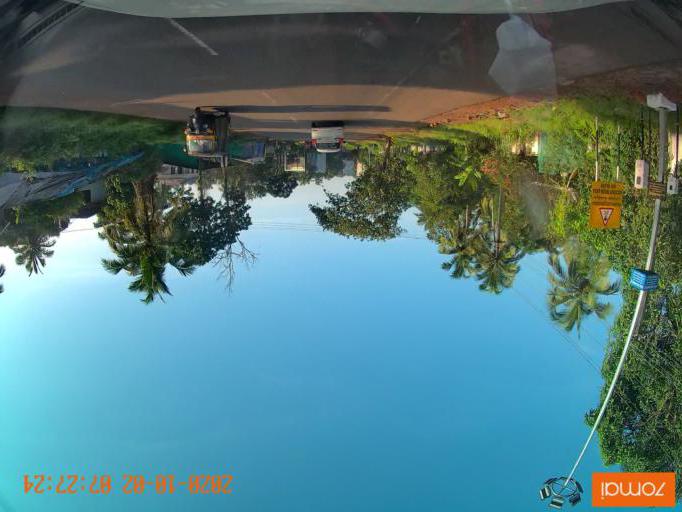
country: IN
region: Kerala
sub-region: Malappuram
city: Pariyapuram
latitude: 11.0237
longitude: 75.9478
